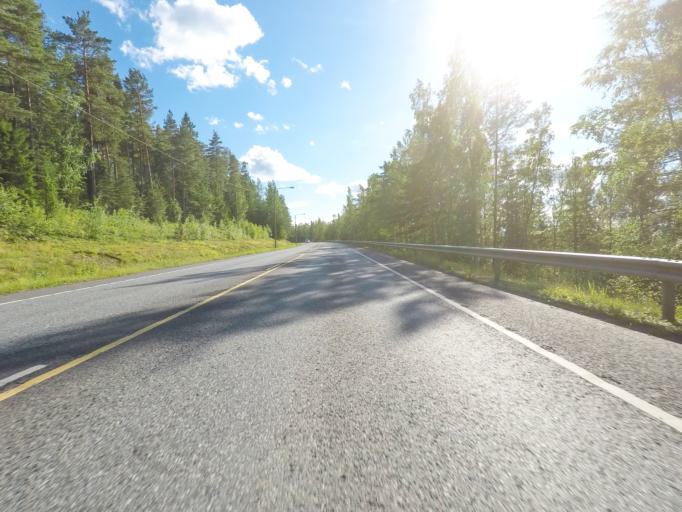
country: FI
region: Uusimaa
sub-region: Helsinki
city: Vihti
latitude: 60.3378
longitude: 24.2946
